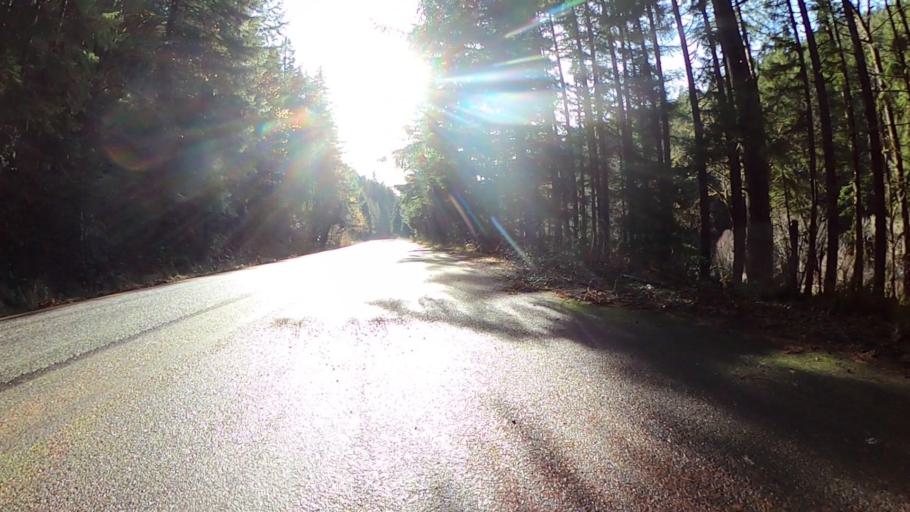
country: US
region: Oregon
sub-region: Lane County
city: Oakridge
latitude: 43.7670
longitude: -122.4888
